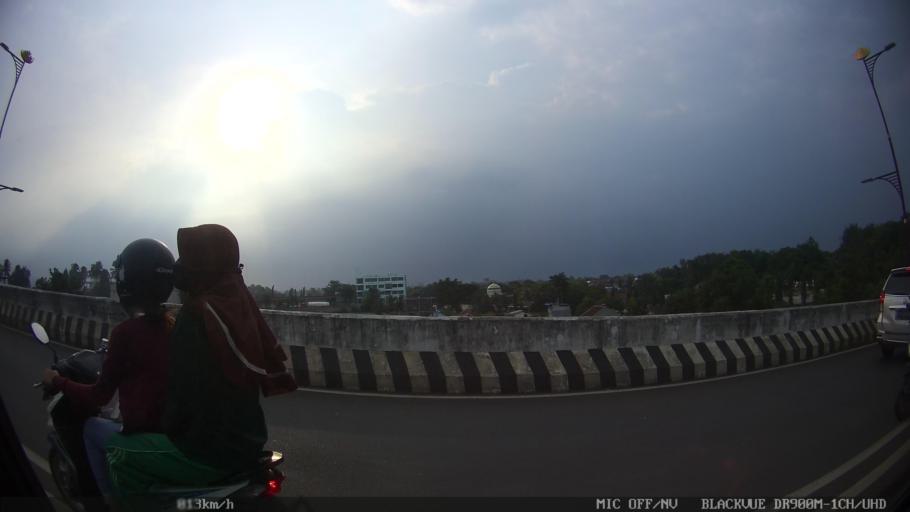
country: ID
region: Lampung
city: Kedaton
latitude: -5.3591
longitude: 105.2361
